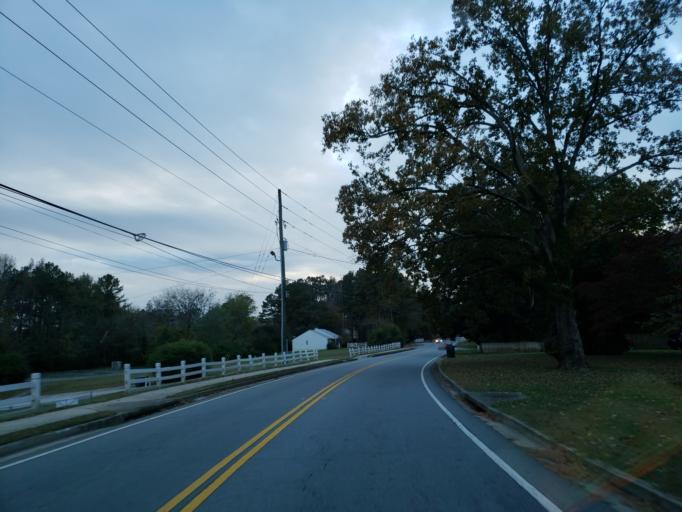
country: US
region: Georgia
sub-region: Cobb County
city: Kennesaw
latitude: 34.0273
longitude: -84.6506
